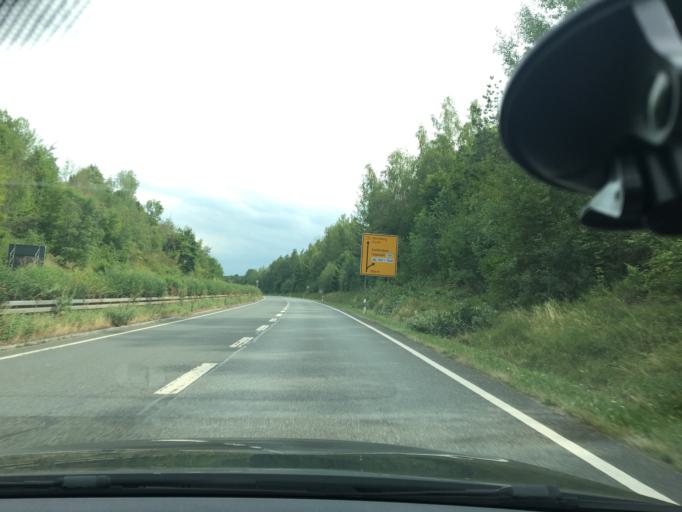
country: DE
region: Bavaria
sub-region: Regierungsbezirk Mittelfranken
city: Langenzenn
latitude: 49.4883
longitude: 10.7776
